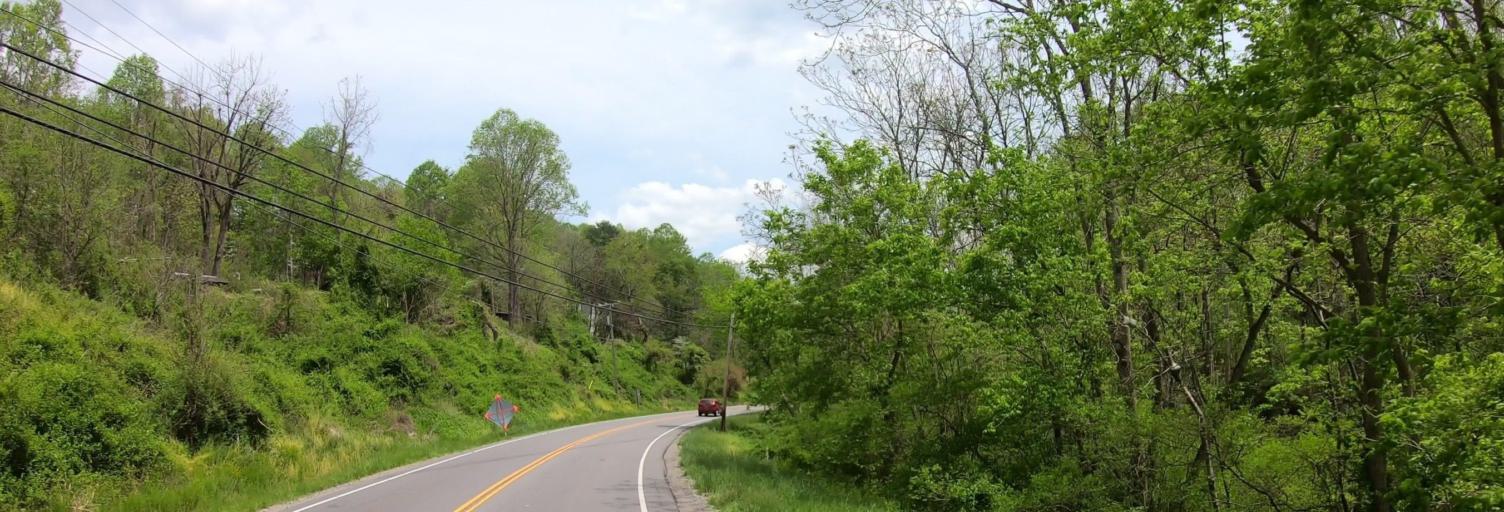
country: US
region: Virginia
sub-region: Roanoke County
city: Cave Spring
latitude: 37.1995
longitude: -80.0623
